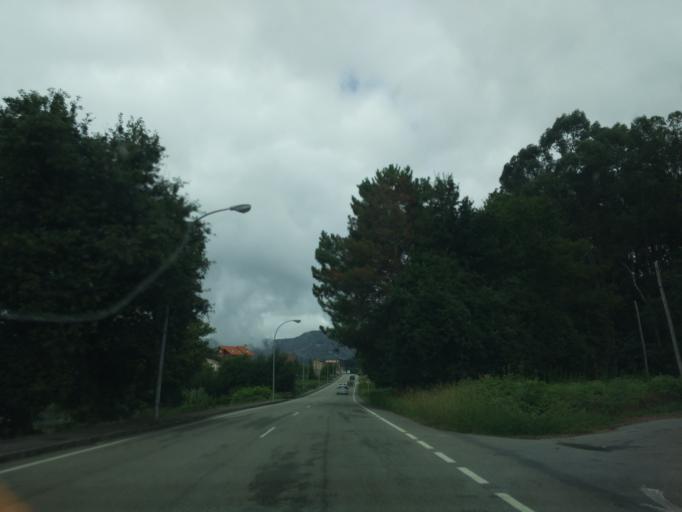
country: ES
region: Galicia
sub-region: Provincia da Coruna
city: Boiro
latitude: 42.6433
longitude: -8.8694
